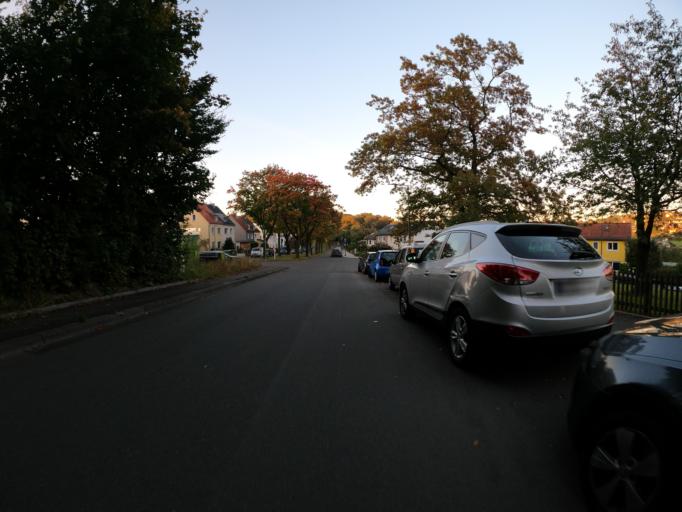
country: DE
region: North Rhine-Westphalia
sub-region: Regierungsbezirk Dusseldorf
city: Wuppertal
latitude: 51.2361
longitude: 7.1402
